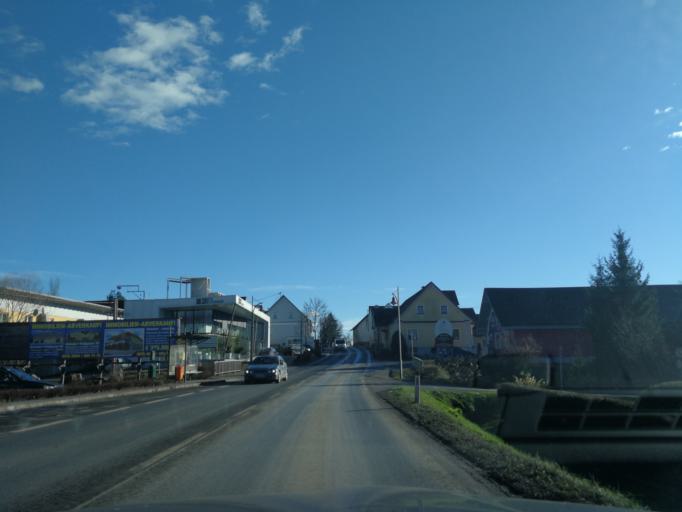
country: AT
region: Styria
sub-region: Politischer Bezirk Weiz
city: Gleisdorf
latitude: 47.0989
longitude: 15.7198
